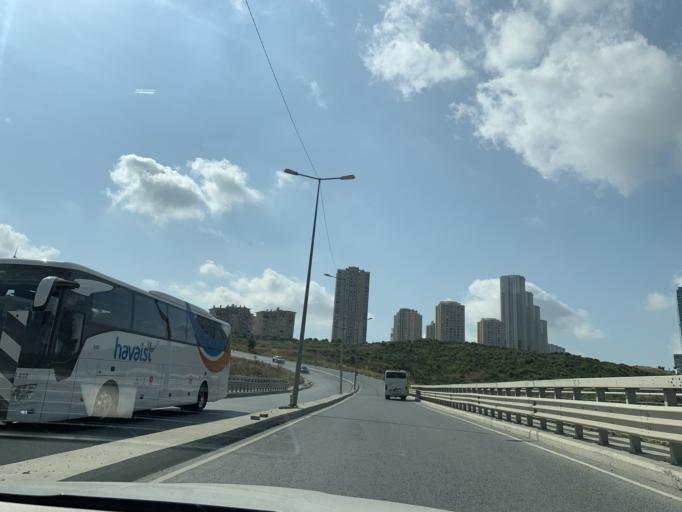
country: TR
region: Istanbul
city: Esenyurt
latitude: 41.0689
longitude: 28.7041
